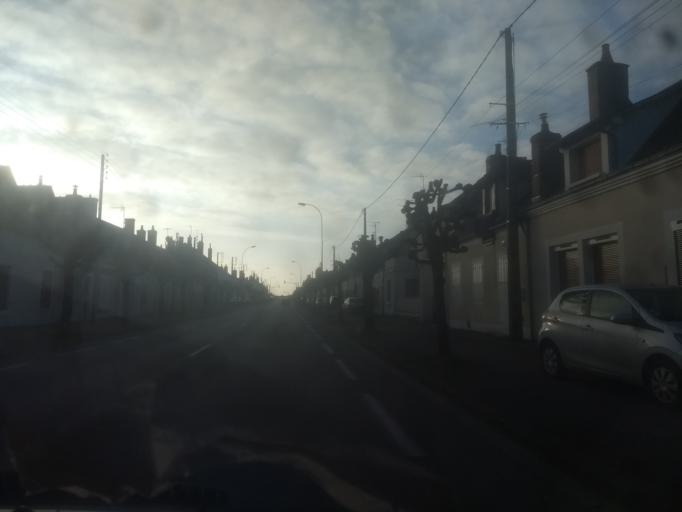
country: FR
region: Centre
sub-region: Departement du Cher
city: Mehun-sur-Yevre
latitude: 47.1493
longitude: 2.2160
